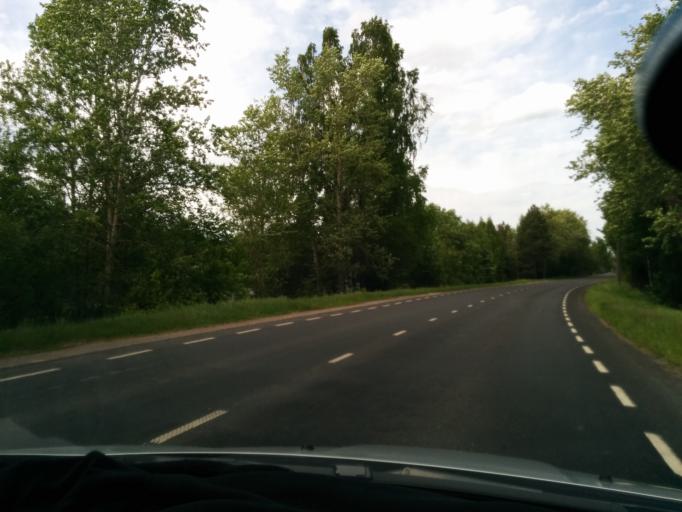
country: EE
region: Harju
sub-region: Loksa linn
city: Loksa
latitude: 59.5706
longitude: 25.7245
